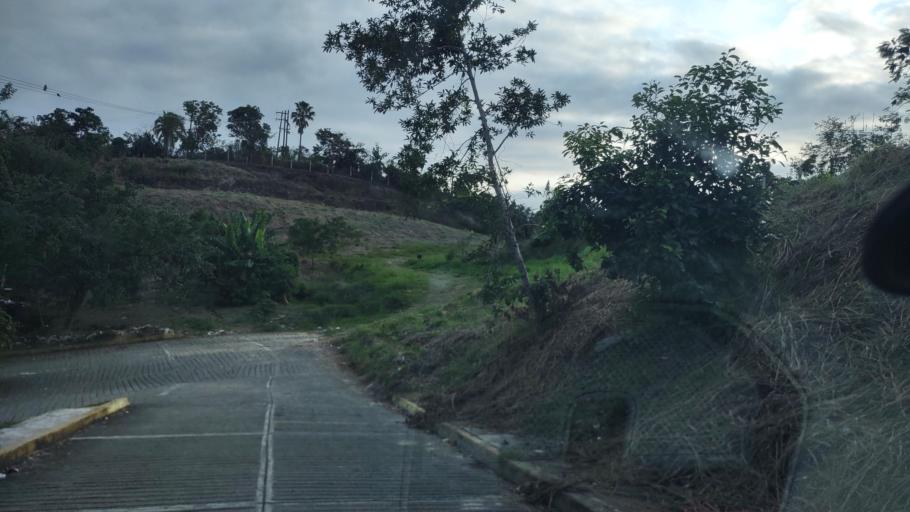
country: MX
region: Veracruz
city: Papantla de Olarte
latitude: 20.4516
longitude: -97.3069
